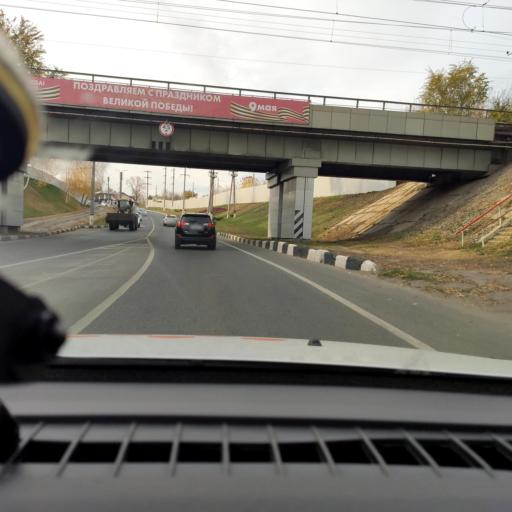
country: RU
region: Samara
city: Novokuybyshevsk
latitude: 53.1189
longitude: 49.9377
